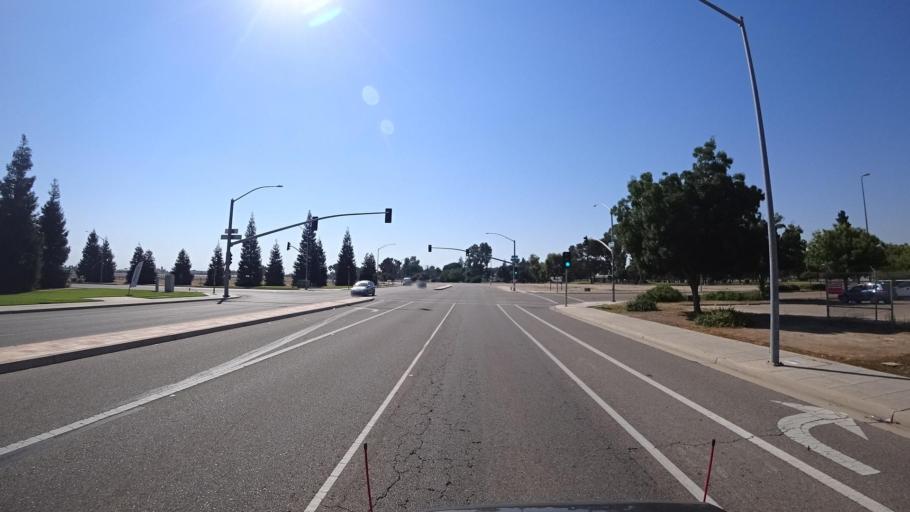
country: US
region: California
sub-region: Fresno County
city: Tarpey Village
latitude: 36.7803
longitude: -119.7111
